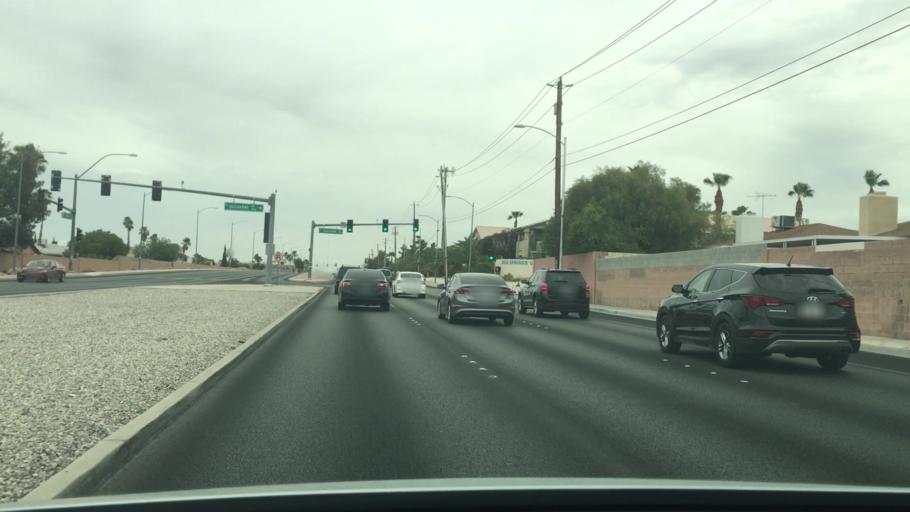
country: US
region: Nevada
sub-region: Clark County
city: Spring Valley
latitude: 36.1709
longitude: -115.2600
